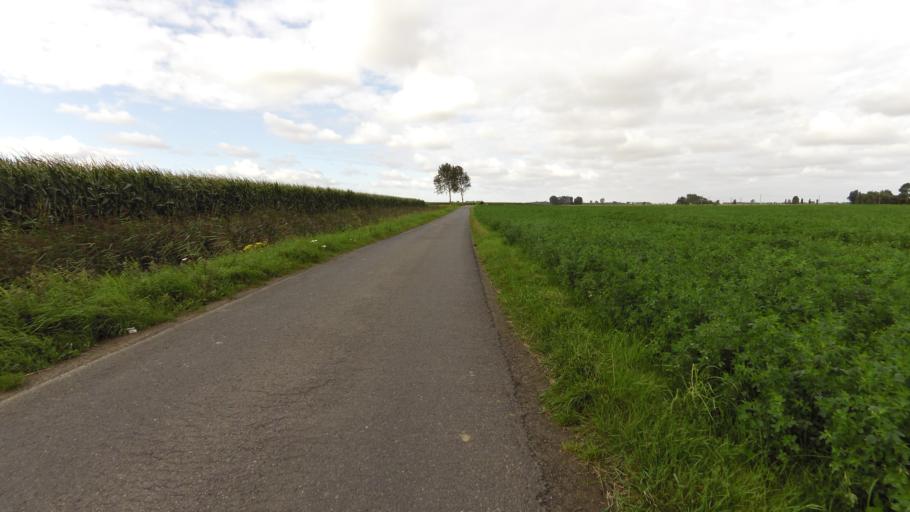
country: BE
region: Flanders
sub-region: Provincie West-Vlaanderen
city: Gistel
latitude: 51.1562
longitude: 2.9234
